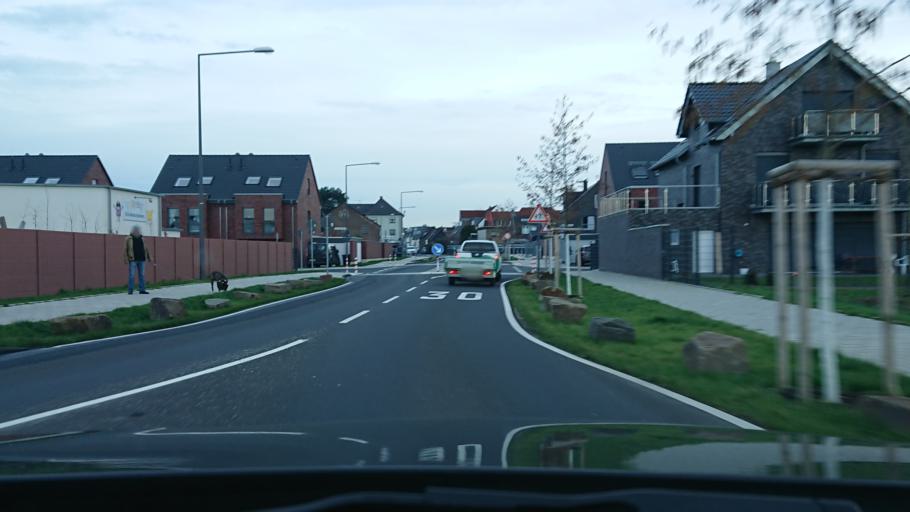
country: DE
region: North Rhine-Westphalia
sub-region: Regierungsbezirk Koln
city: Sinnersdorf
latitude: 51.0484
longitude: 6.8443
